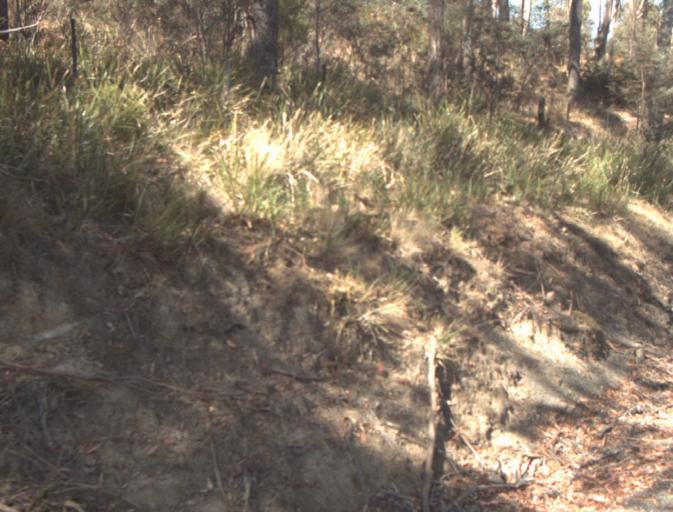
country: AU
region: Tasmania
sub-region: Launceston
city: Newstead
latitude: -41.3678
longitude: 147.3021
